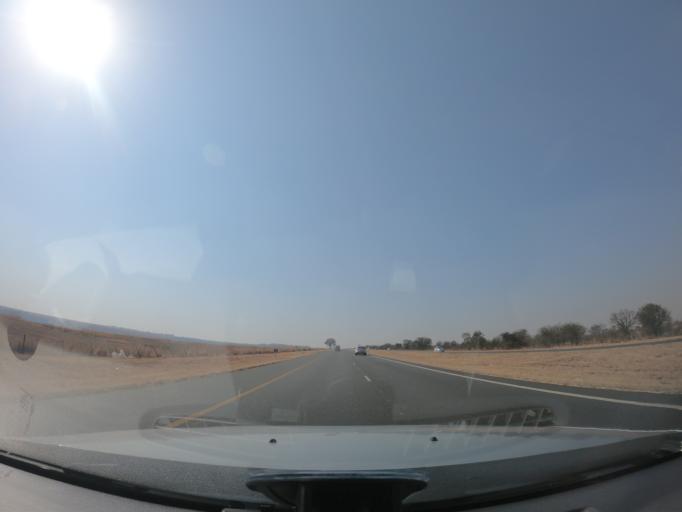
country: ZA
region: Mpumalanga
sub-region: Nkangala District Municipality
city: Witbank
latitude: -25.8696
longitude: 29.0348
